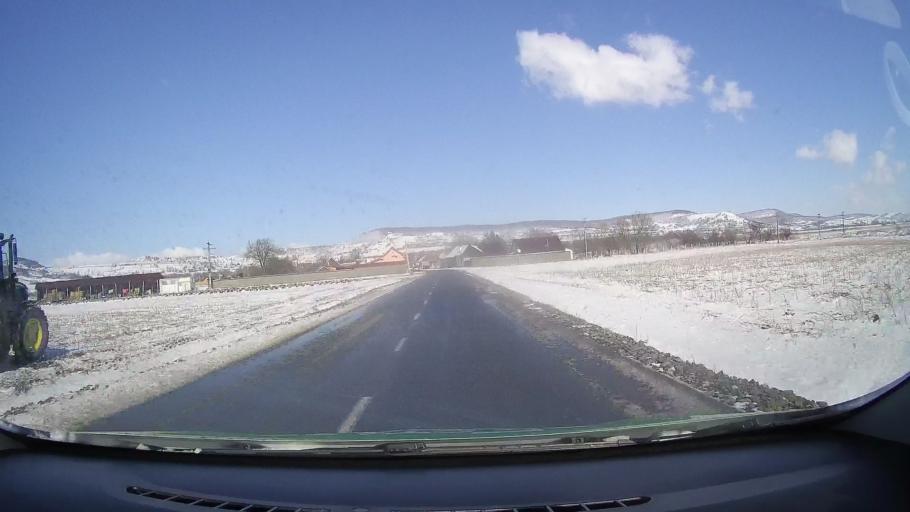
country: RO
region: Sibiu
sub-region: Comuna Avrig
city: Avrig
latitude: 45.7532
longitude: 24.3917
